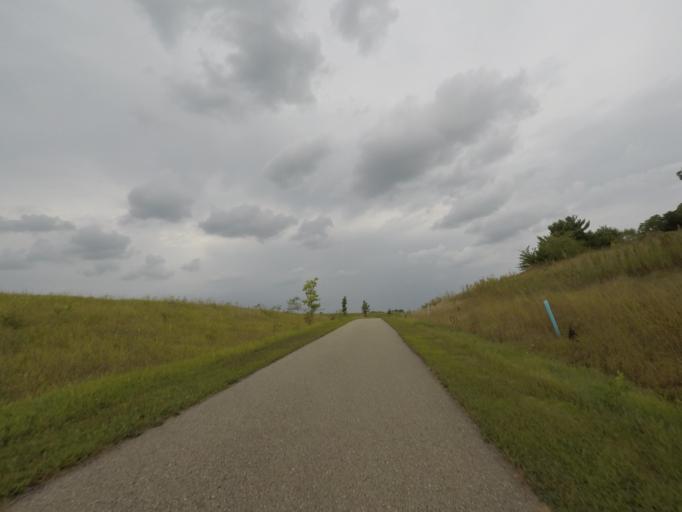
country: US
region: Wisconsin
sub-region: Jefferson County
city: Jefferson
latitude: 42.9847
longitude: -88.8287
